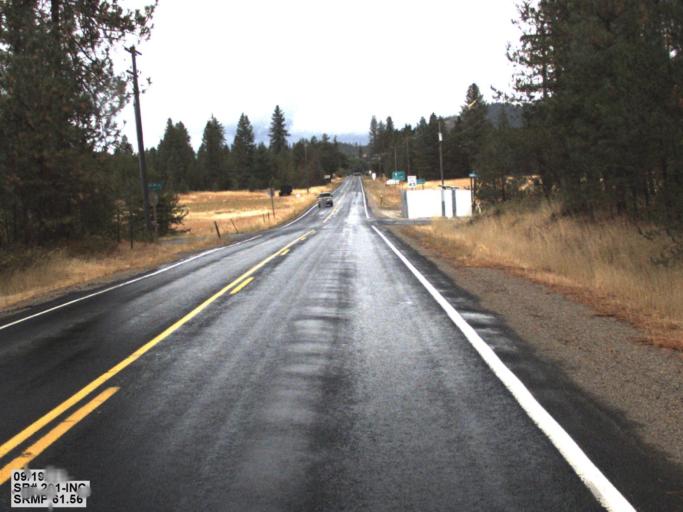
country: US
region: Washington
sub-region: Stevens County
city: Chewelah
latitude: 48.0483
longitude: -117.7415
